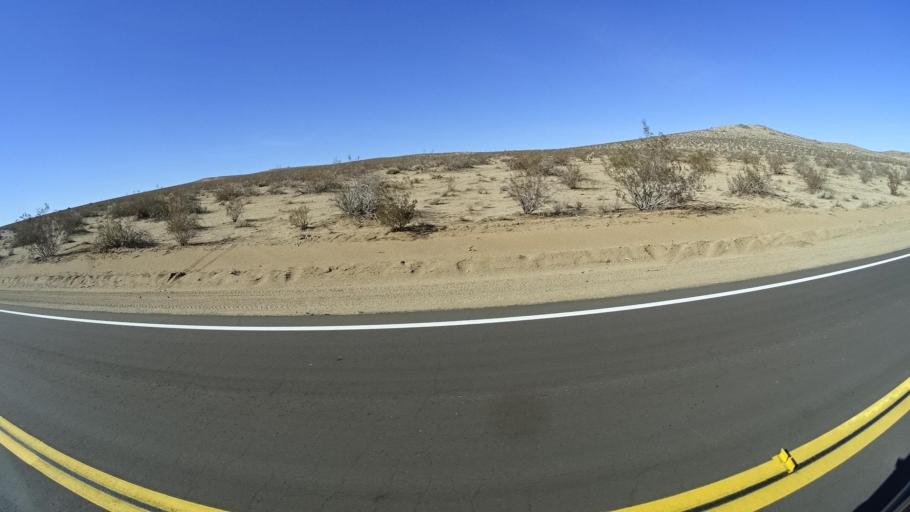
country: US
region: California
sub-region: Kern County
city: Ridgecrest
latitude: 35.5295
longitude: -117.5941
